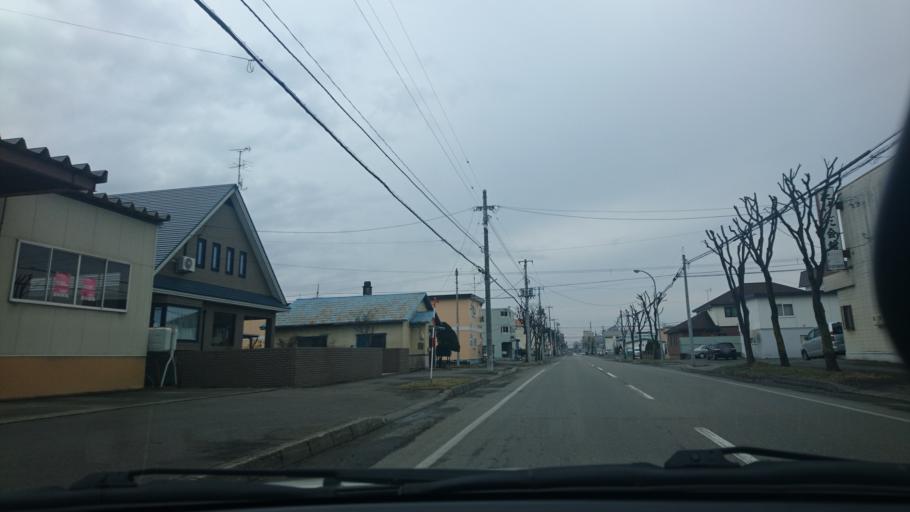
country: JP
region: Hokkaido
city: Obihiro
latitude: 42.9349
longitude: 143.1957
